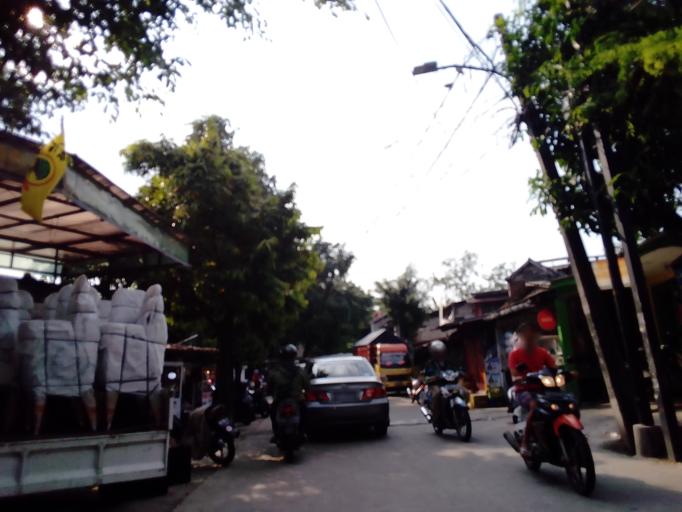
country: ID
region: Jakarta Raya
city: Jakarta
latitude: -6.2586
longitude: 106.7917
